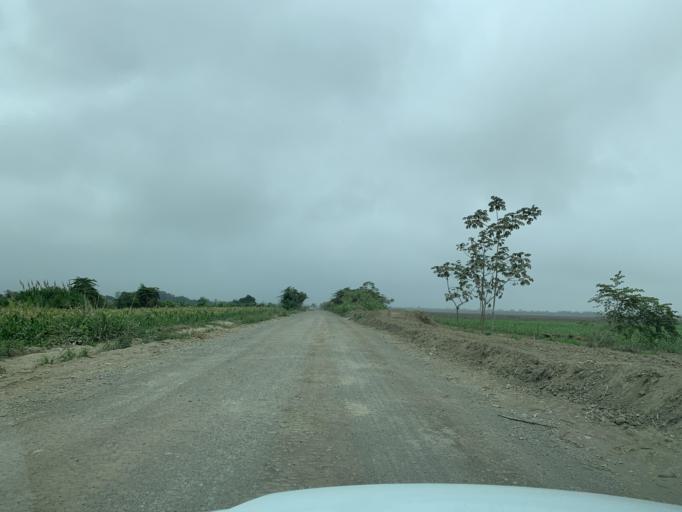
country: EC
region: Guayas
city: Coronel Marcelino Mariduena
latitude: -2.3597
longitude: -79.5509
